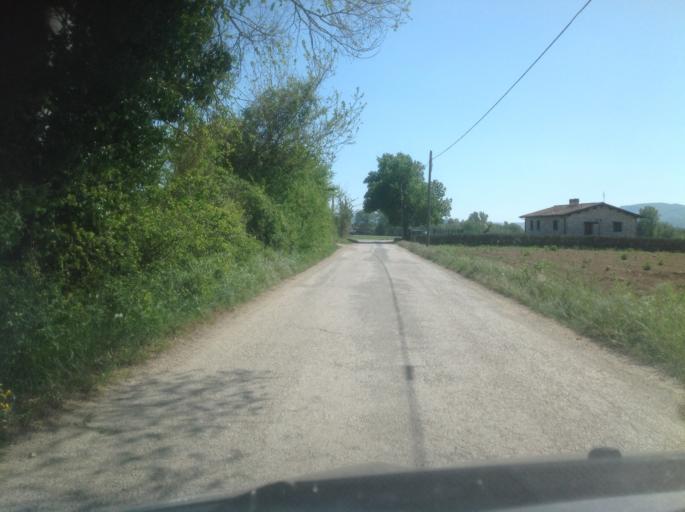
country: IT
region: Latium
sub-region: Provincia di Rieti
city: Colli sul Velino
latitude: 42.4906
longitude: 12.8028
